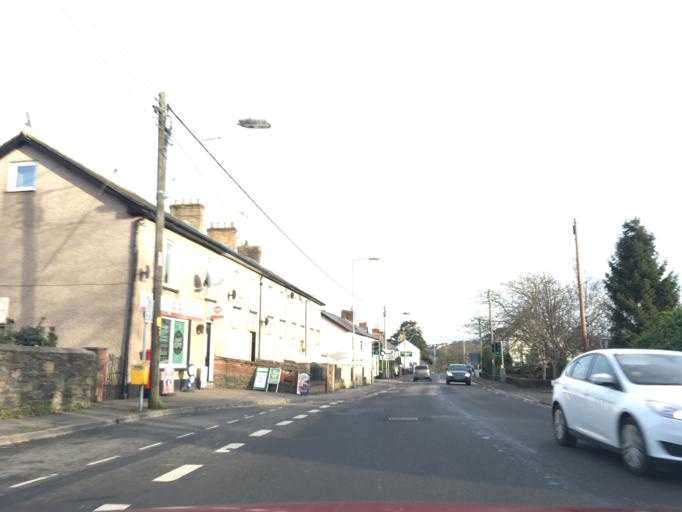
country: GB
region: Wales
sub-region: Newport
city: Newport
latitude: 51.5775
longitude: -3.0476
